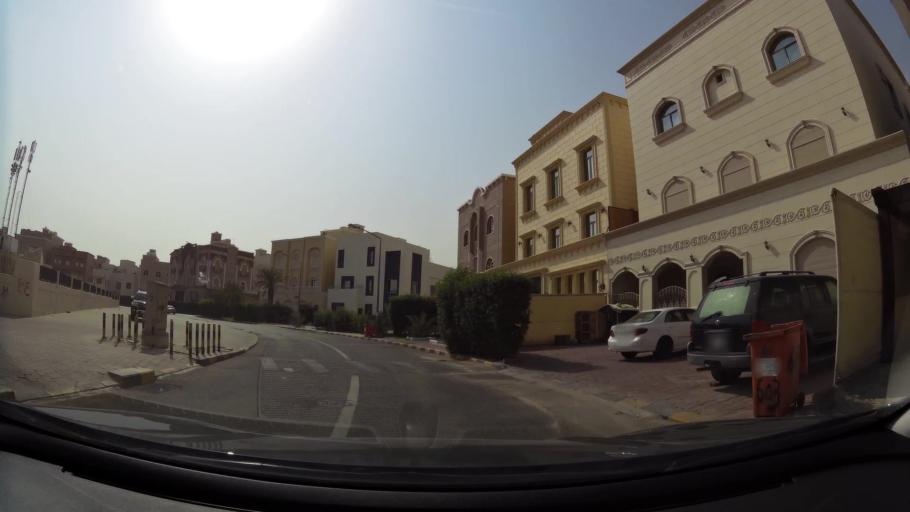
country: KW
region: Muhafazat al Jahra'
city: Al Jahra'
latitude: 29.3337
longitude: 47.7604
